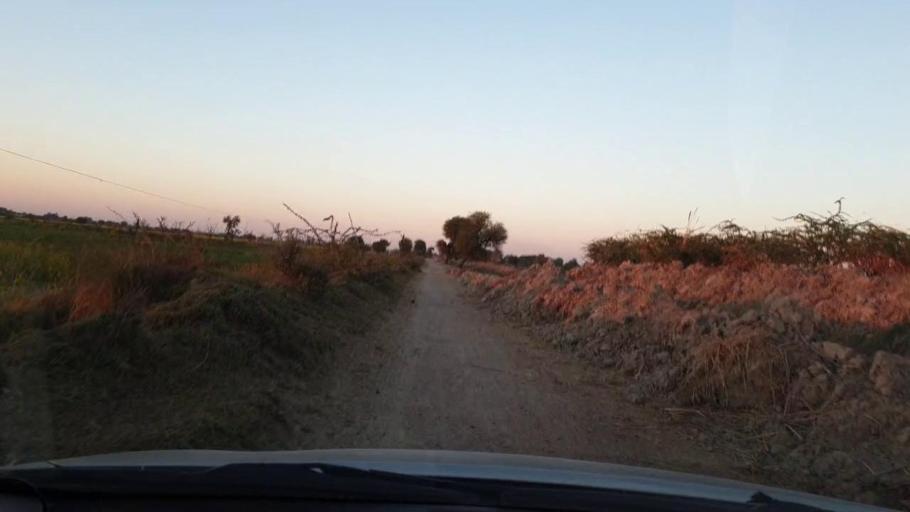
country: PK
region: Sindh
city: Jhol
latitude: 25.9077
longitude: 68.8857
